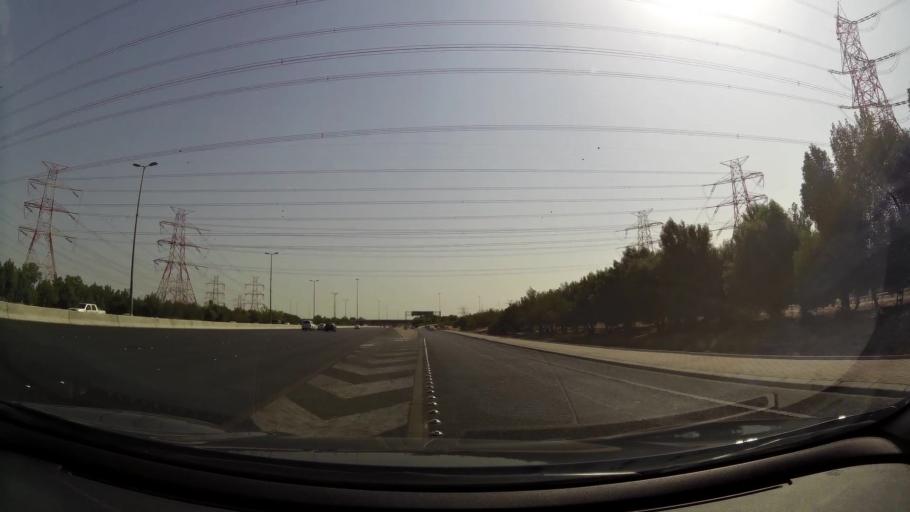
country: KW
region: Mubarak al Kabir
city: Sabah as Salim
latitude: 29.2708
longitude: 48.0394
